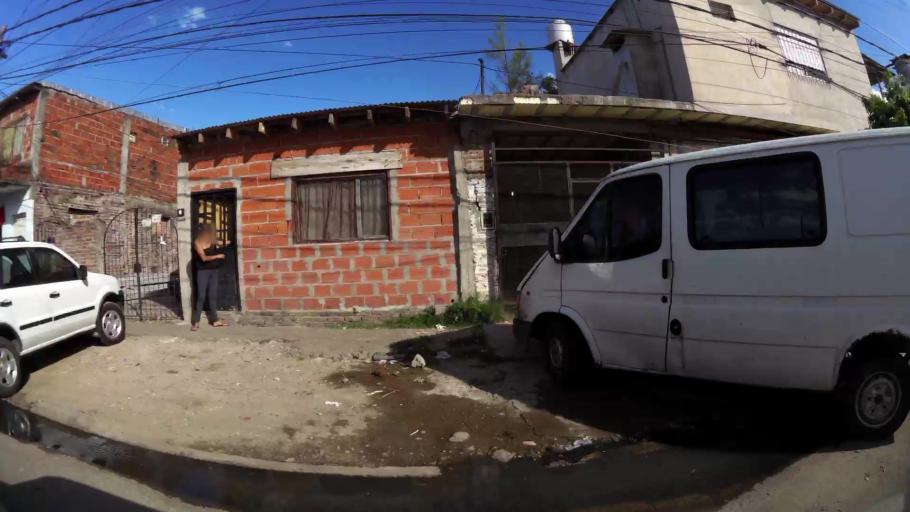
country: AR
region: Buenos Aires
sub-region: Partido de General San Martin
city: General San Martin
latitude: -34.5498
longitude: -58.5408
